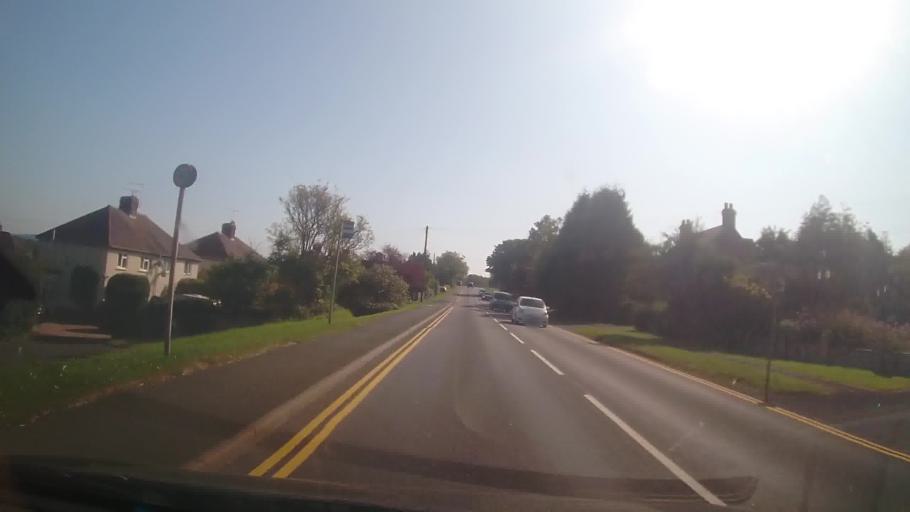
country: GB
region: England
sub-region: Worcestershire
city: Badsey
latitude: 52.0685
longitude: -1.9012
